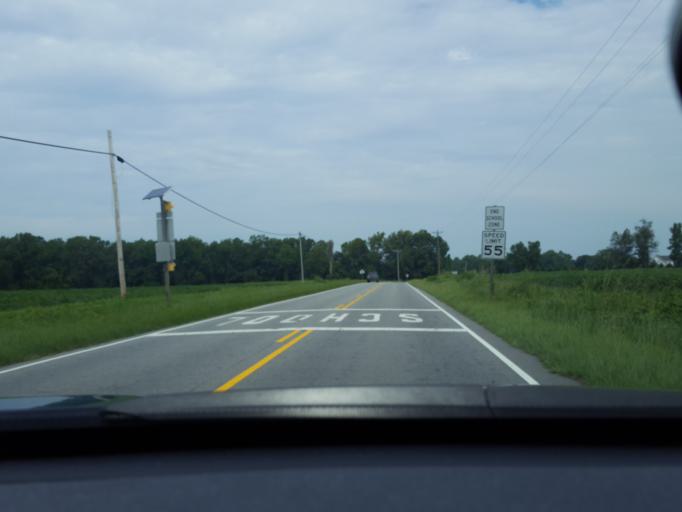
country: US
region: North Carolina
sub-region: Chowan County
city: Edenton
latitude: 36.1651
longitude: -76.6575
